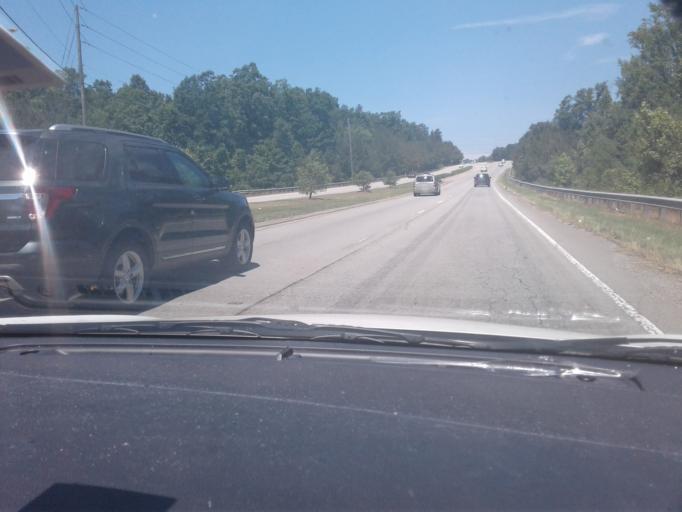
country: US
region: North Carolina
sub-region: Wake County
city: Holly Springs
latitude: 35.6210
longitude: -78.8171
